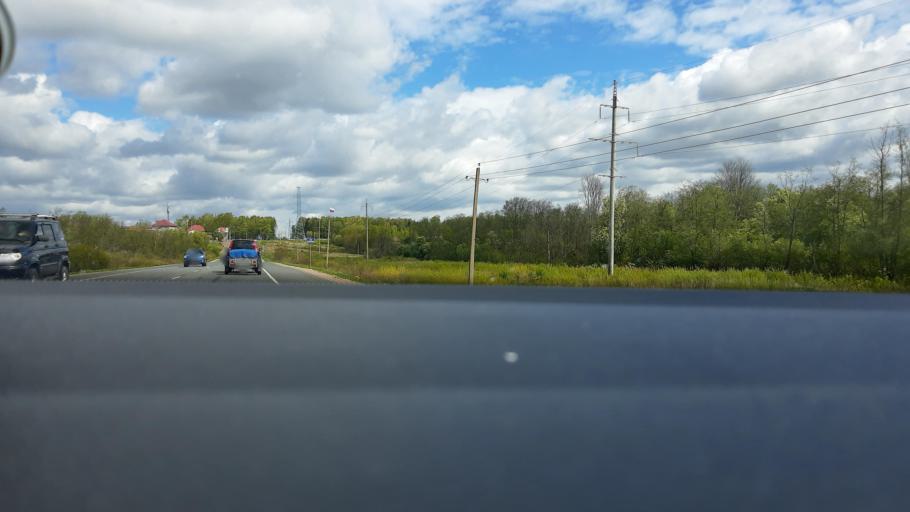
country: RU
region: Moskovskaya
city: Dmitrov
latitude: 56.3519
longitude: 37.4864
